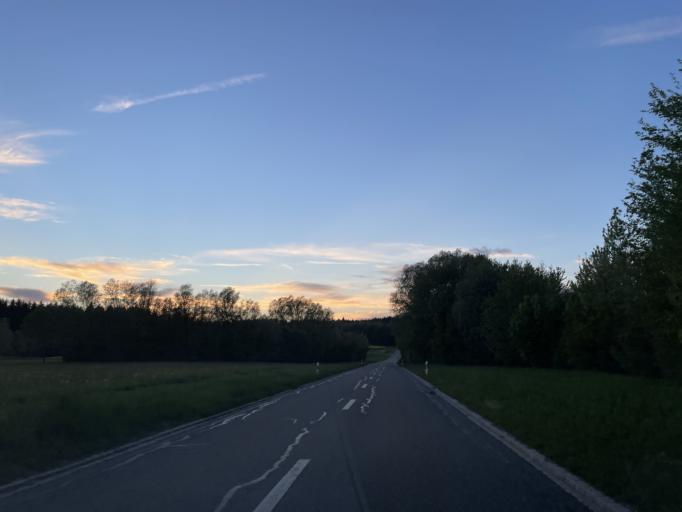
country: CH
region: Zurich
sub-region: Bezirk Winterthur
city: Brutten
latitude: 47.4597
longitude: 8.6835
